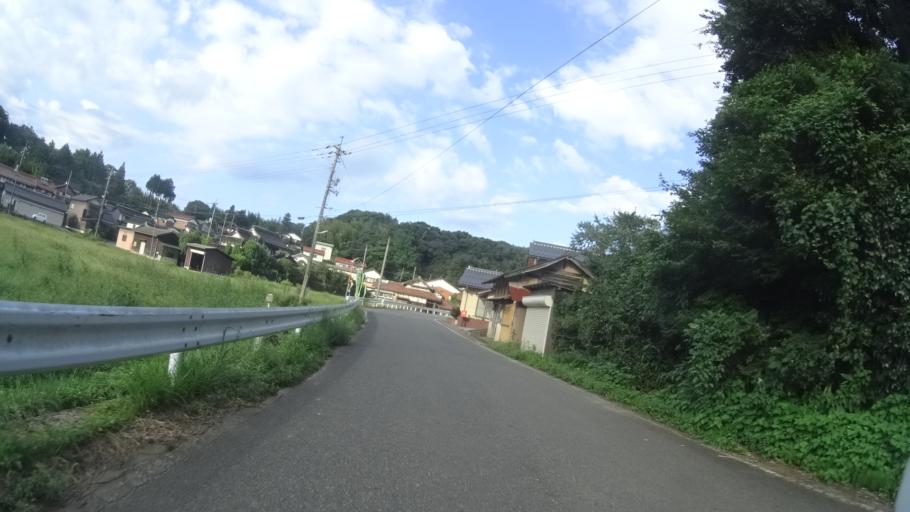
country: JP
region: Tottori
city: Kurayoshi
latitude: 35.4851
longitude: 133.9004
